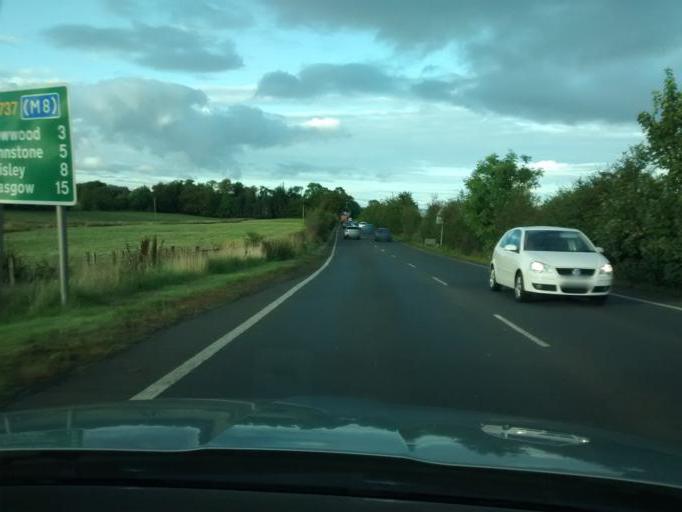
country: GB
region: Scotland
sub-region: Renfrewshire
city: Lochwinnoch
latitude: 55.7867
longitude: -4.6058
